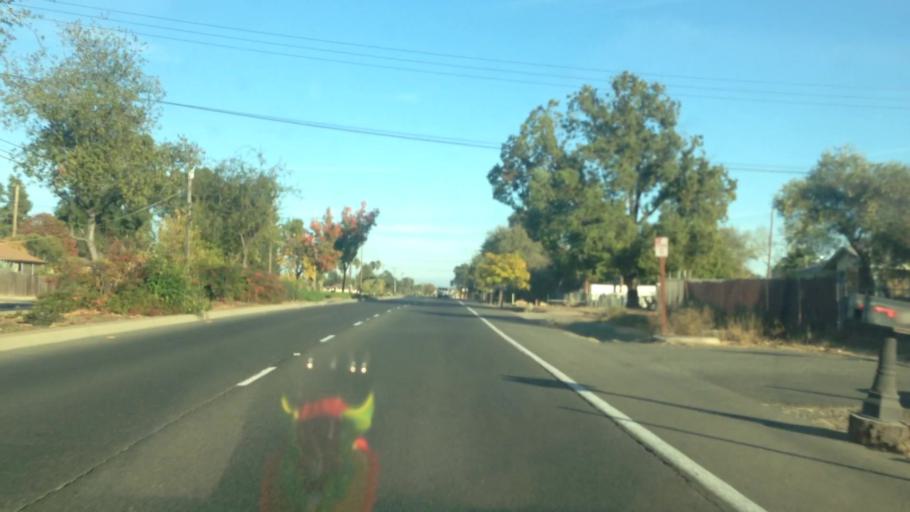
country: US
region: California
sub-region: Sacramento County
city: Rio Linda
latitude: 38.6906
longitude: -121.4179
